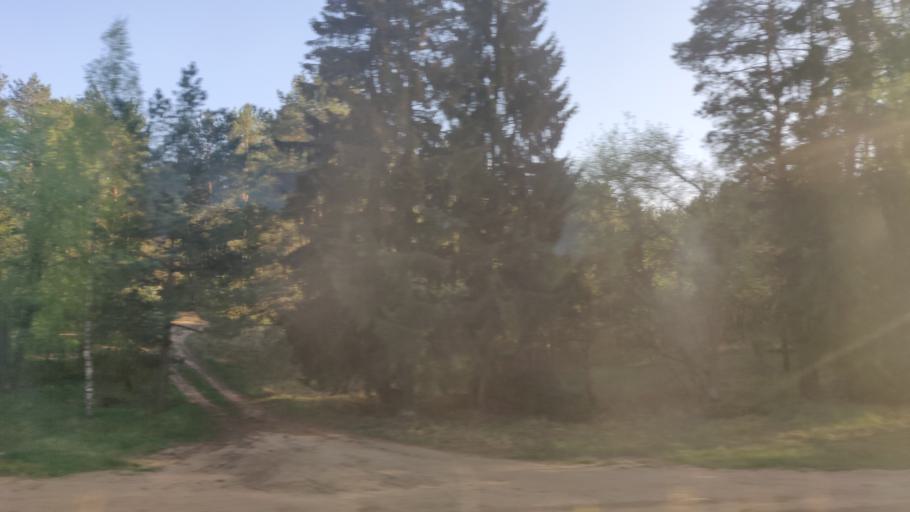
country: LT
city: Baltoji Voke
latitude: 54.6293
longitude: 25.1596
